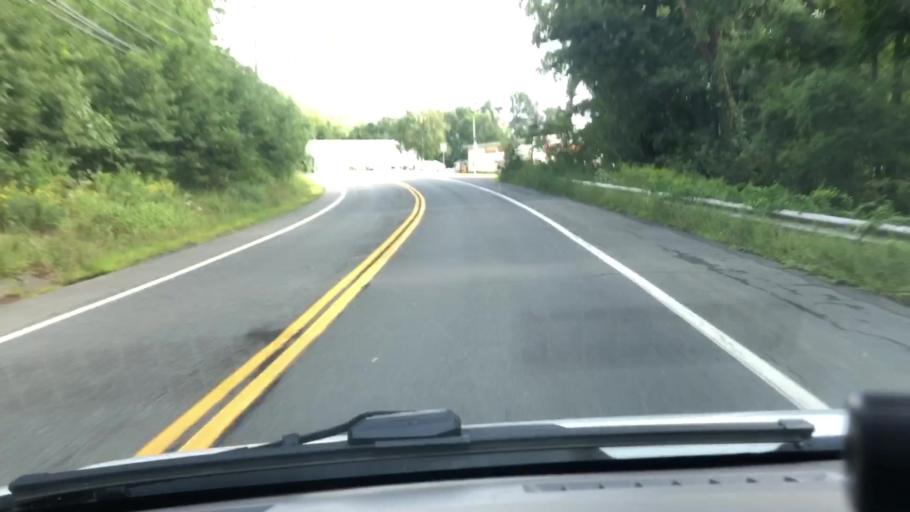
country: US
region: Massachusetts
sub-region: Franklin County
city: Shelburne Falls
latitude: 42.5932
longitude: -72.7256
